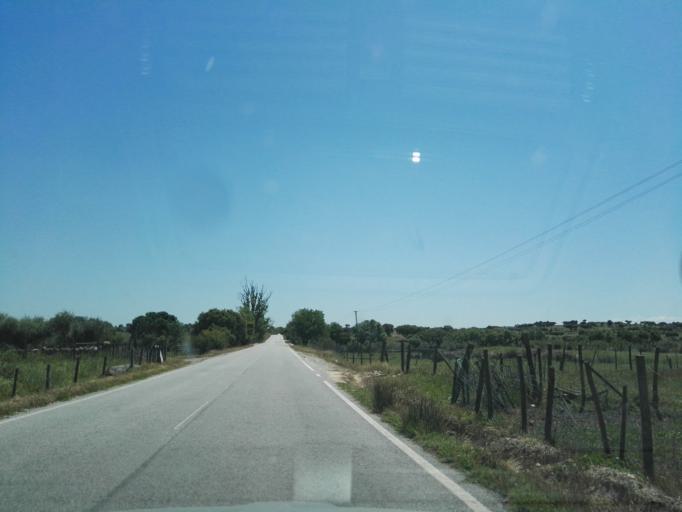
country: PT
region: Portalegre
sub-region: Arronches
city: Arronches
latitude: 39.0097
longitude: -7.2410
